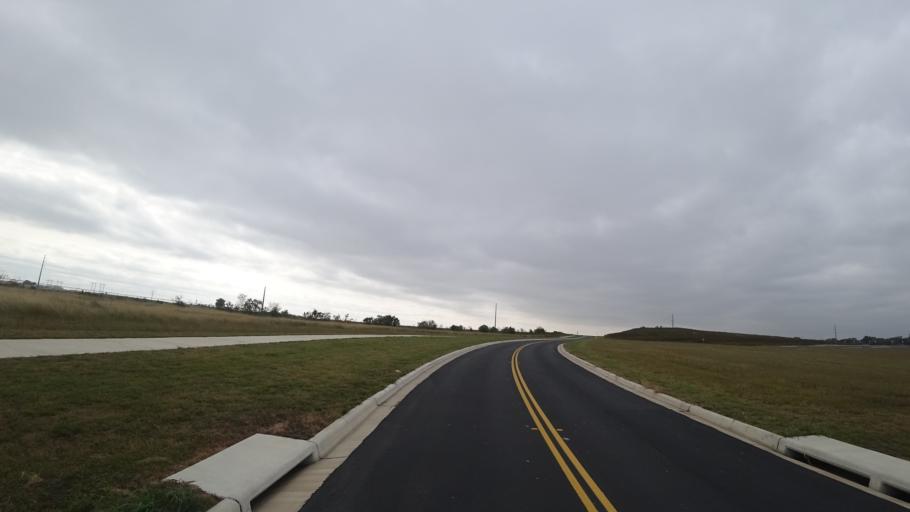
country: US
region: Texas
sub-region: Travis County
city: Pflugerville
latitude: 30.4124
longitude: -97.5905
